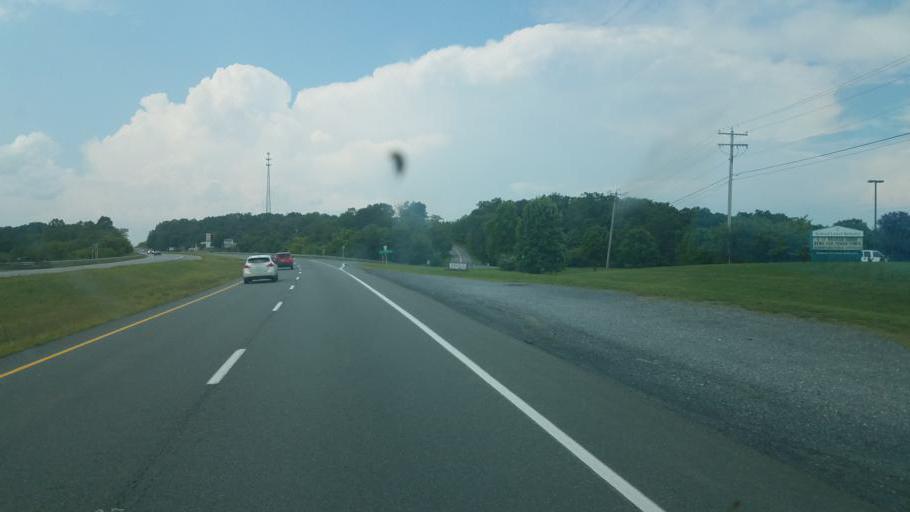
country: US
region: Virginia
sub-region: Frederick County
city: Shawnee Land
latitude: 39.3137
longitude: -78.2899
